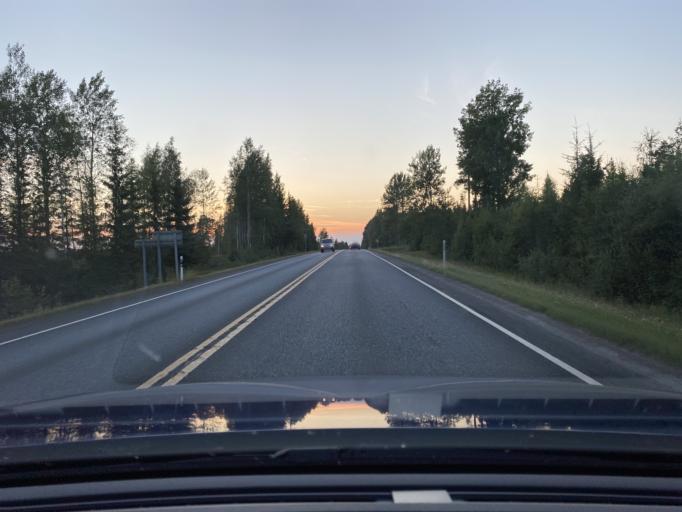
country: FI
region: Pirkanmaa
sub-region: Luoteis-Pirkanmaa
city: Ikaalinen
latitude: 61.7914
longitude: 22.9870
